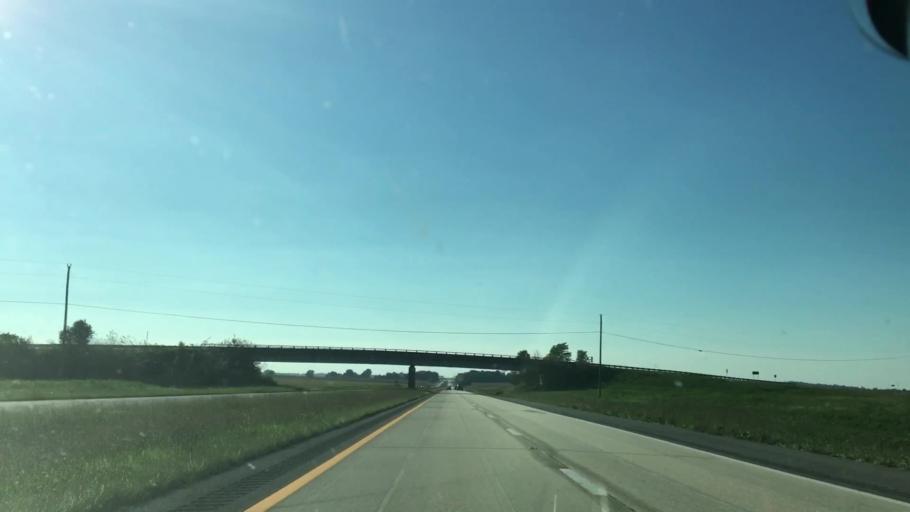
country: US
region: Kentucky
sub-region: Henderson County
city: Henderson
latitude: 37.7855
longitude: -87.4696
